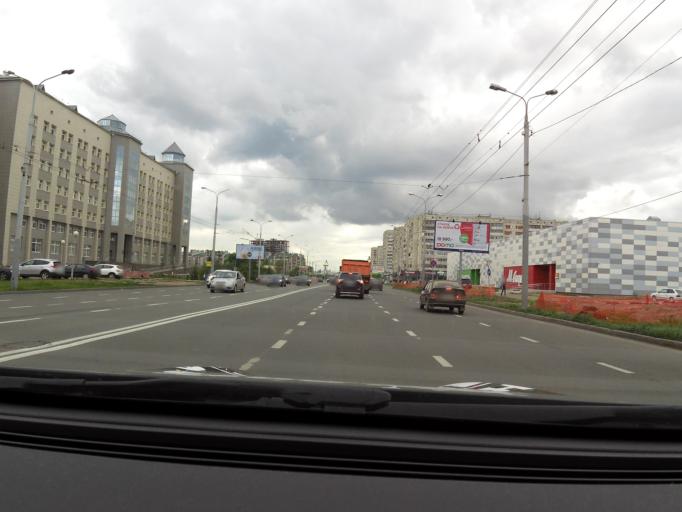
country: RU
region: Tatarstan
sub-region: Gorod Kazan'
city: Kazan
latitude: 55.8174
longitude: 49.0953
